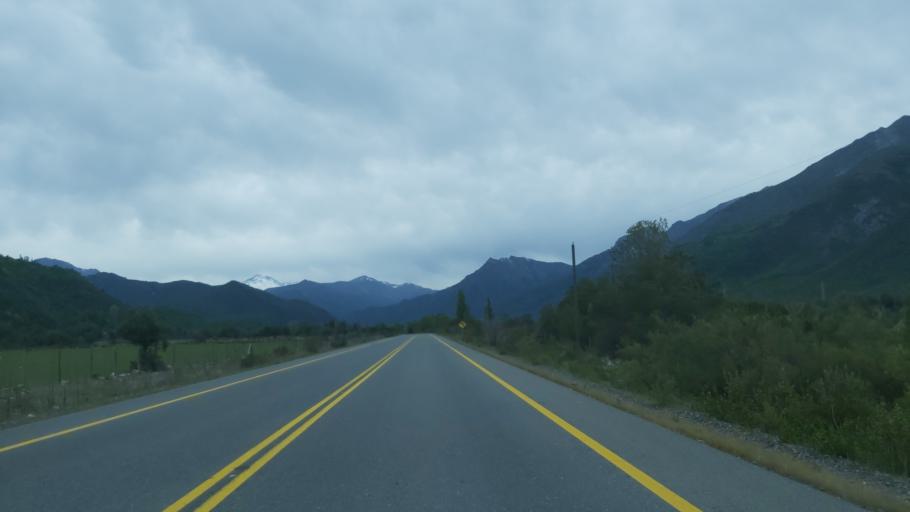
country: CL
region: Maule
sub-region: Provincia de Linares
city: Colbun
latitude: -35.7357
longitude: -71.0116
